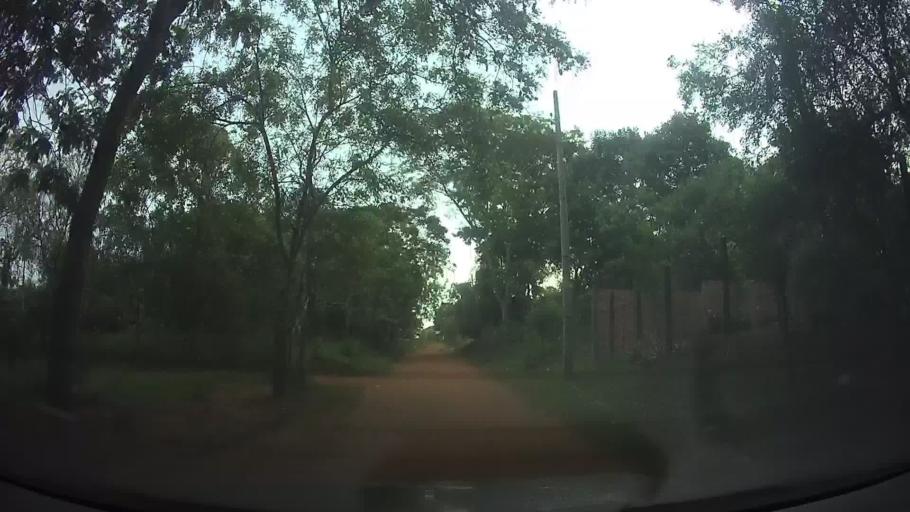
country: PY
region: Central
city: Limpio
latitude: -25.2423
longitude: -57.4485
